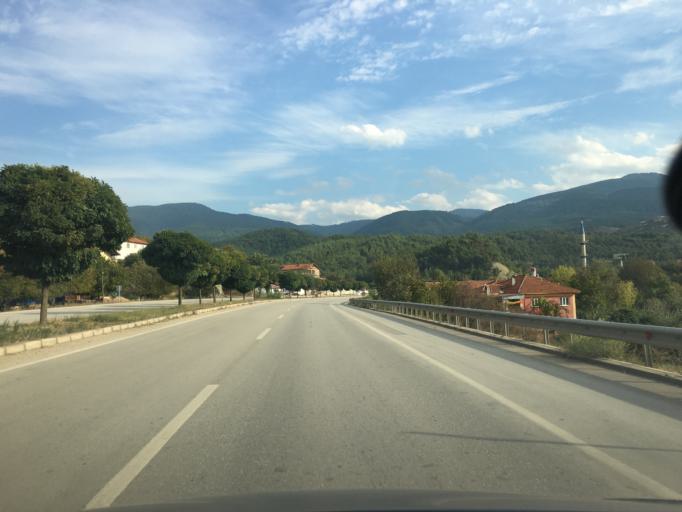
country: TR
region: Karabuk
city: Karabuk
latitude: 41.0961
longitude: 32.6765
